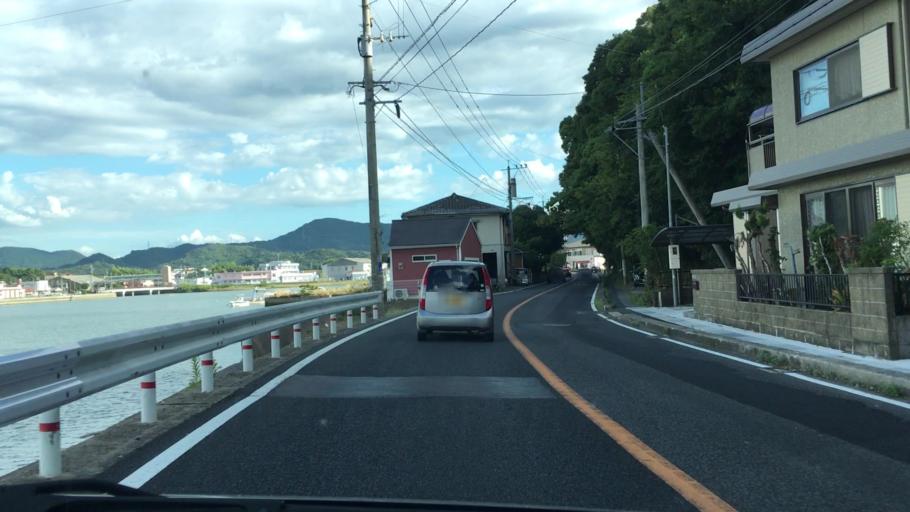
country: JP
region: Nagasaki
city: Sasebo
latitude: 33.1353
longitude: 129.7952
